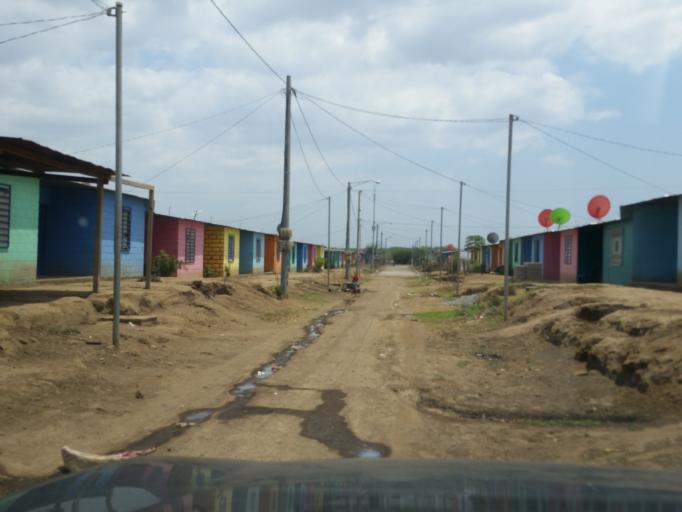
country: NI
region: Managua
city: Managua
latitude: 12.1280
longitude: -86.1589
